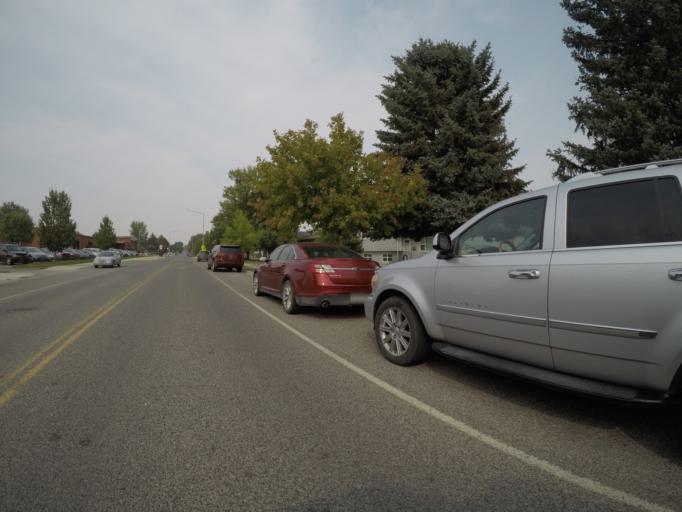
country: US
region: Montana
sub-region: Yellowstone County
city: Laurel
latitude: 45.6728
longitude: -108.7820
